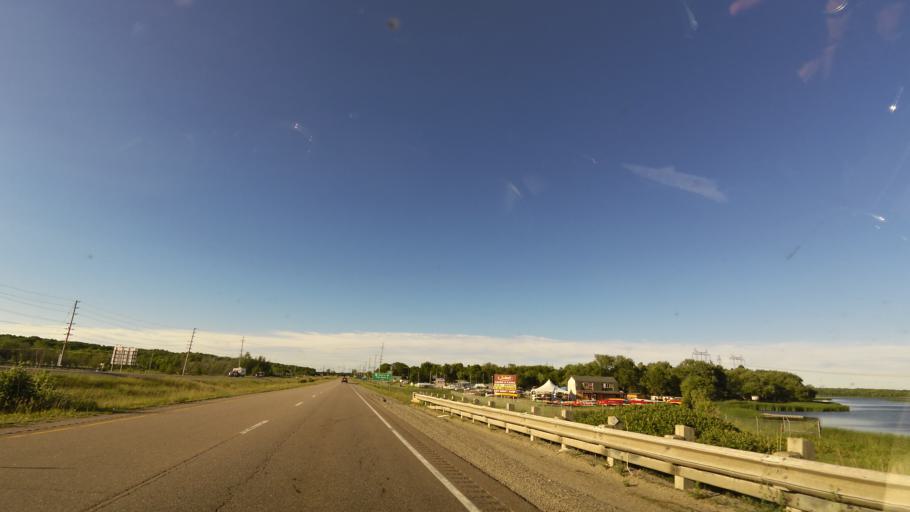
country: CA
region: Ontario
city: Midland
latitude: 44.7584
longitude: -79.6993
